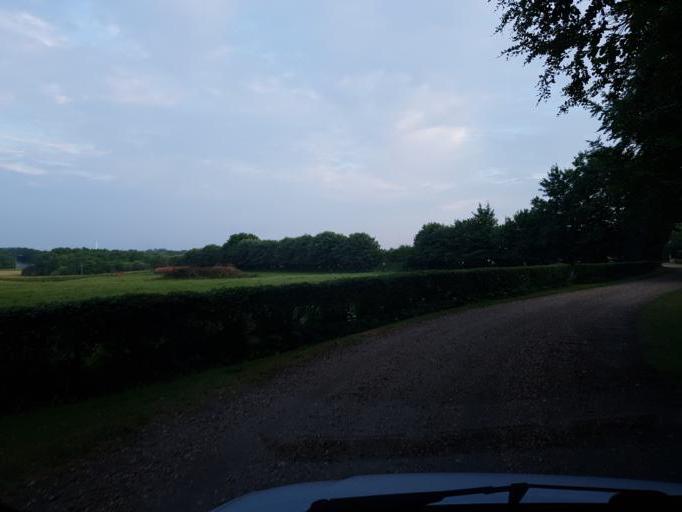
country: DK
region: South Denmark
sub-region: Esbjerg Kommune
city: Esbjerg
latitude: 55.5022
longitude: 8.4775
